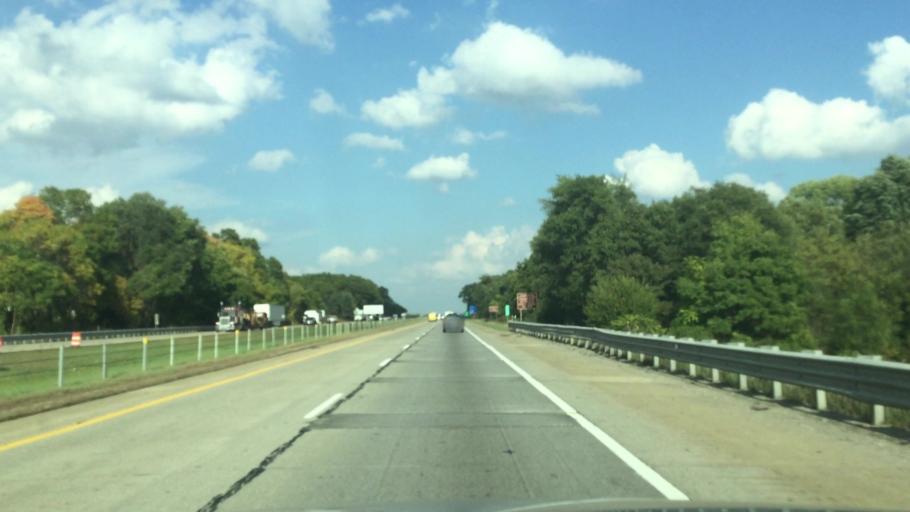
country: US
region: Michigan
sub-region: Calhoun County
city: Battle Creek
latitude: 42.2740
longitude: -85.1686
